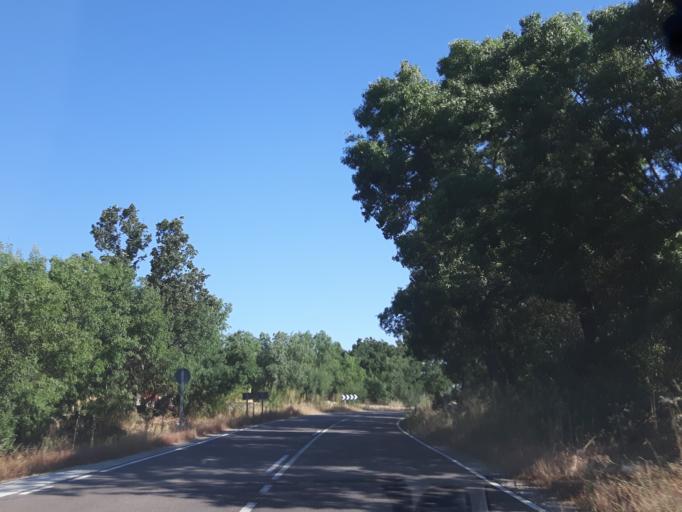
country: ES
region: Castille and Leon
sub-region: Provincia de Salamanca
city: Valdehijaderos
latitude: 40.4267
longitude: -5.8219
